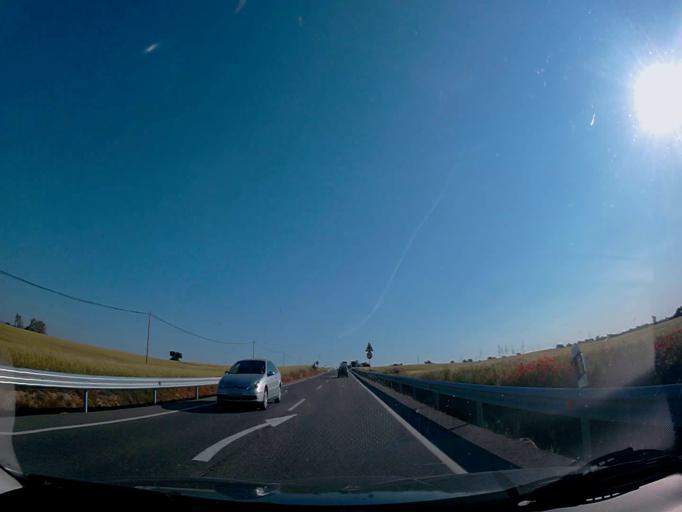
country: ES
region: Castille-La Mancha
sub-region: Province of Toledo
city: Escalona
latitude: 40.1250
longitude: -4.4073
